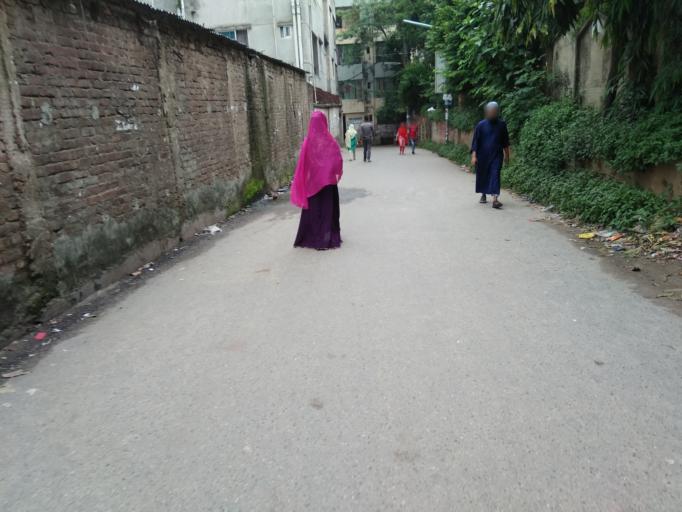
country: BD
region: Dhaka
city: Tungi
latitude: 23.8204
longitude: 90.3595
